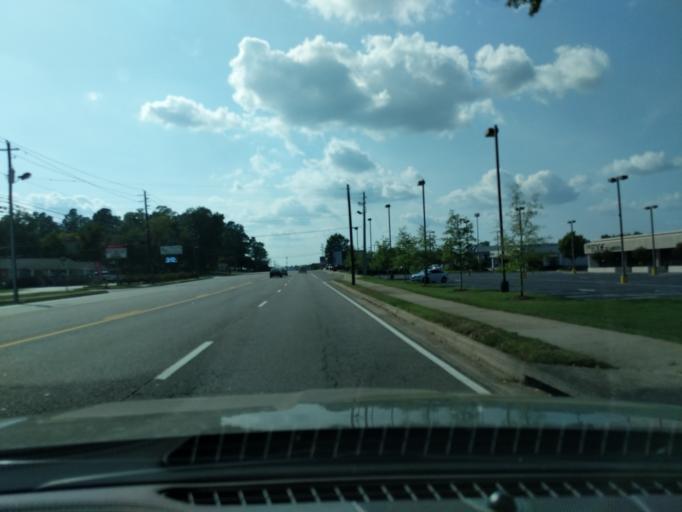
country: US
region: Georgia
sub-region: Columbia County
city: Martinez
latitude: 33.5149
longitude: -82.0623
